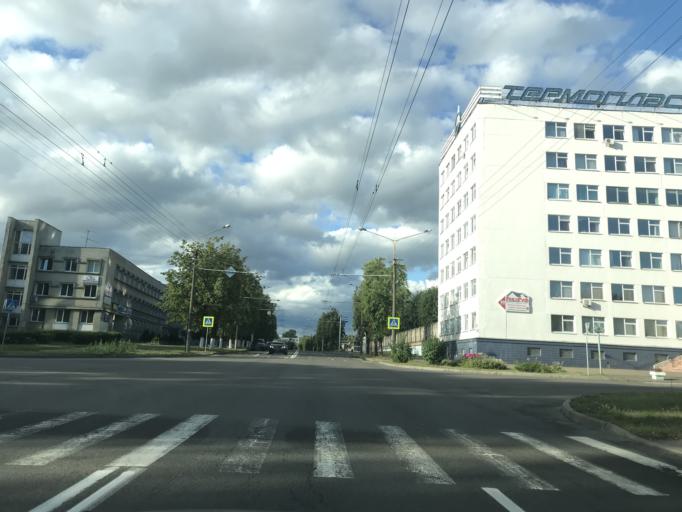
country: BY
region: Minsk
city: Minsk
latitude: 53.9441
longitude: 27.6212
